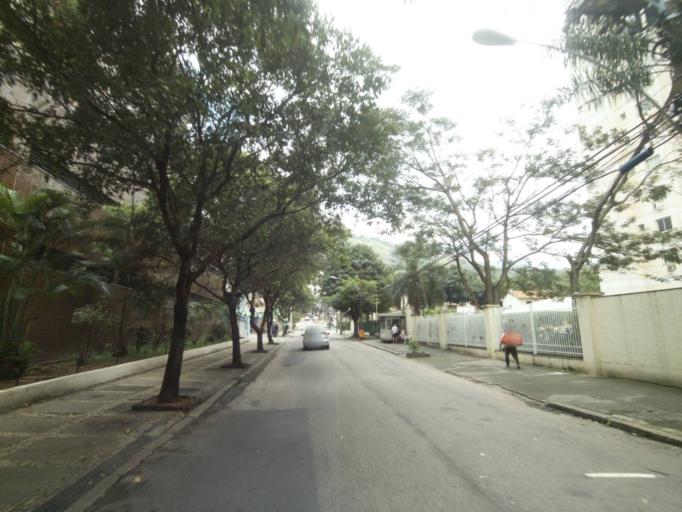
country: BR
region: Rio de Janeiro
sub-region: Rio De Janeiro
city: Rio de Janeiro
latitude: -22.9320
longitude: -43.2469
